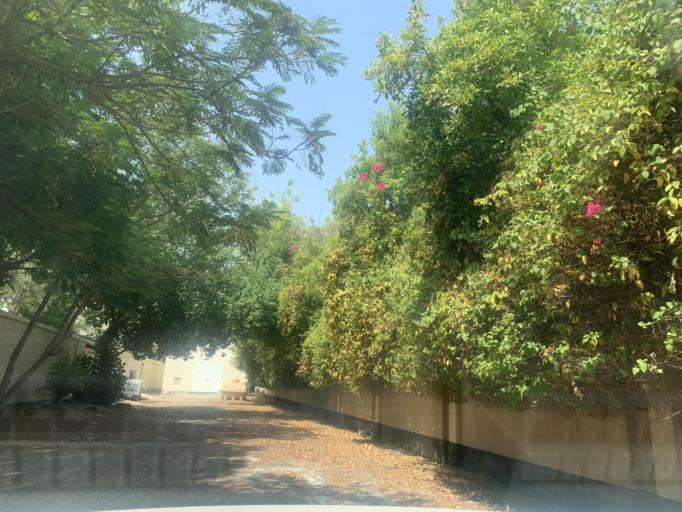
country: BH
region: Central Governorate
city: Madinat Hamad
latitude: 26.1663
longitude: 50.4576
